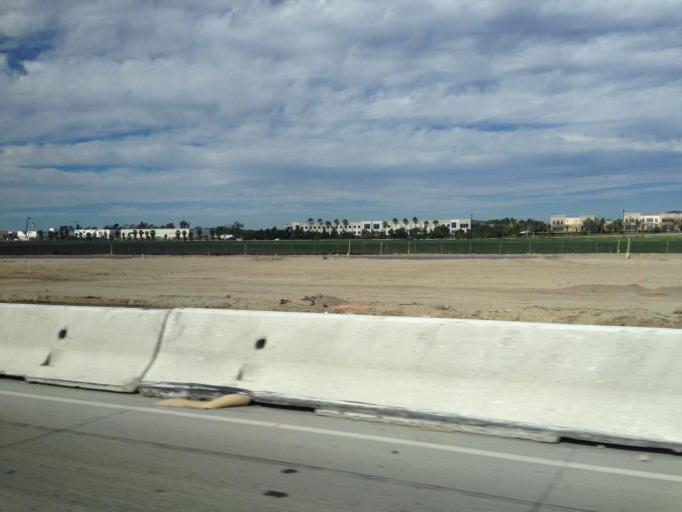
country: MX
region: Baja California
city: Tijuana
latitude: 32.5643
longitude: -116.9549
